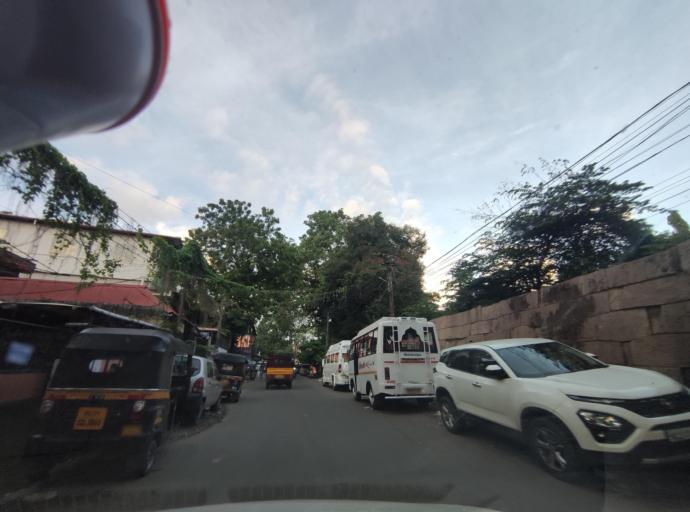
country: IN
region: Kerala
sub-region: Thiruvananthapuram
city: Thiruvananthapuram
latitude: 8.4867
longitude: 76.9396
